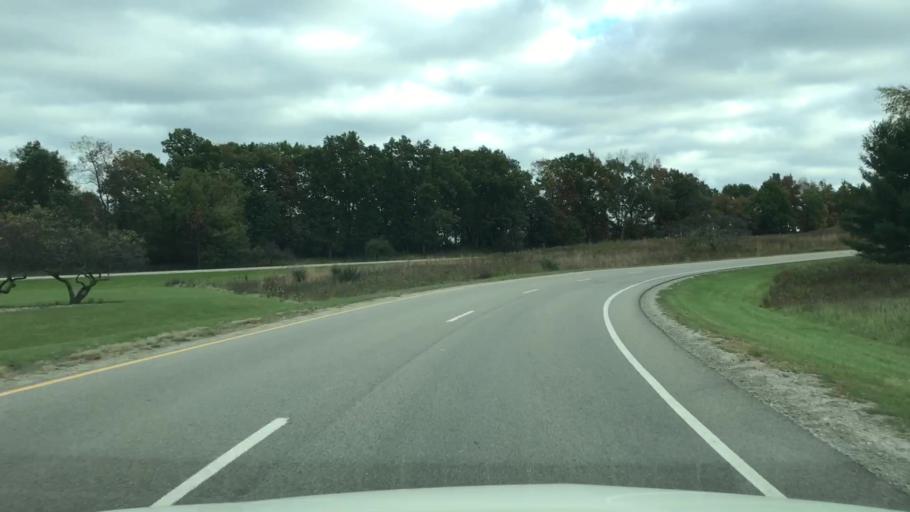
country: US
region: Michigan
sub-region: Macomb County
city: Shelby
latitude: 42.7202
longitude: -83.0727
